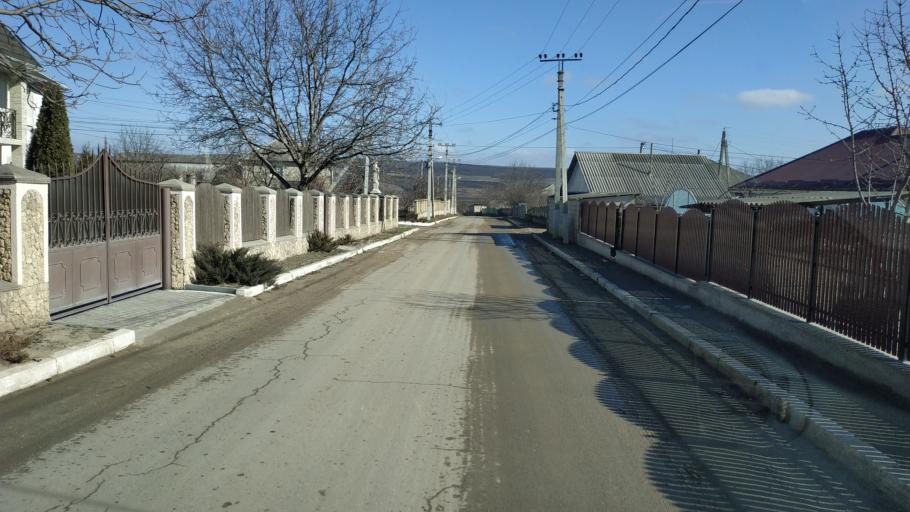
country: MD
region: Hincesti
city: Hincesti
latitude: 46.9327
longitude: 28.6367
